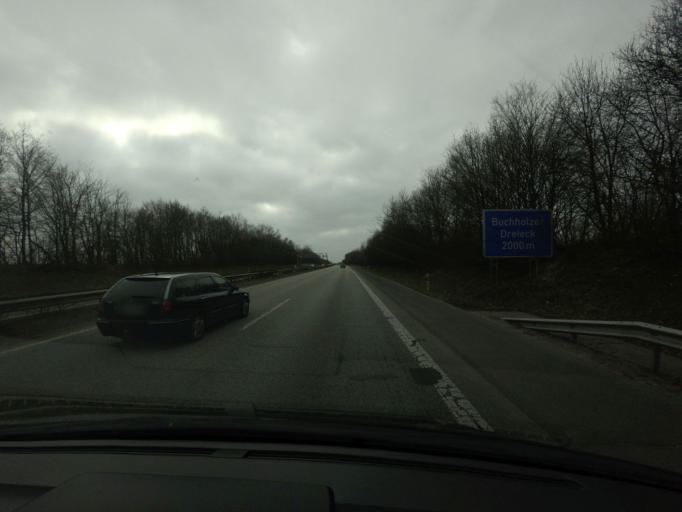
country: DE
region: Lower Saxony
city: Buchholz in der Nordheide
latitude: 53.3900
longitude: 9.8813
